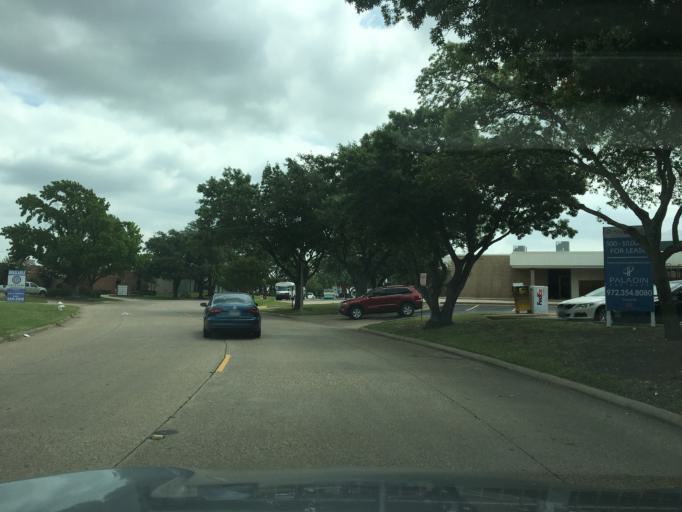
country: US
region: Texas
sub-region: Dallas County
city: Addison
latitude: 32.9365
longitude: -96.8383
